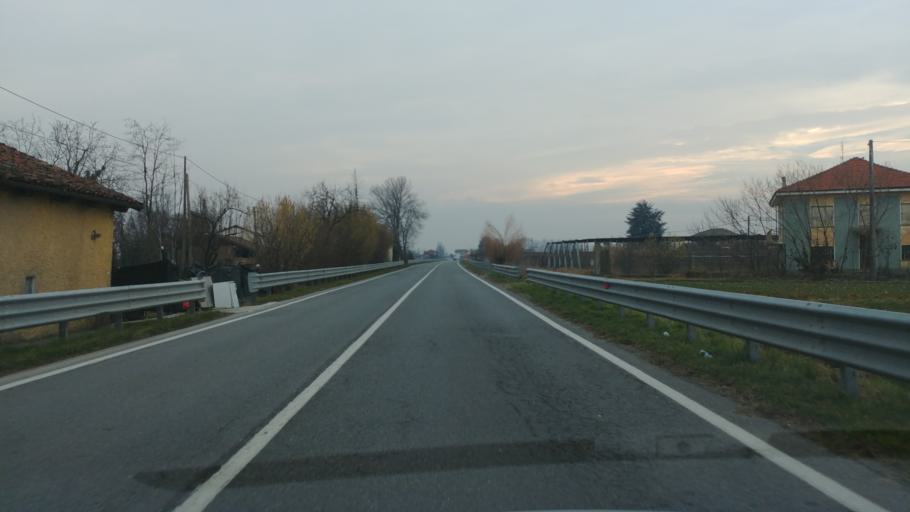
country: IT
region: Piedmont
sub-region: Provincia di Cuneo
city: Sant'Albano Stura
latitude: 44.5076
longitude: 7.6837
